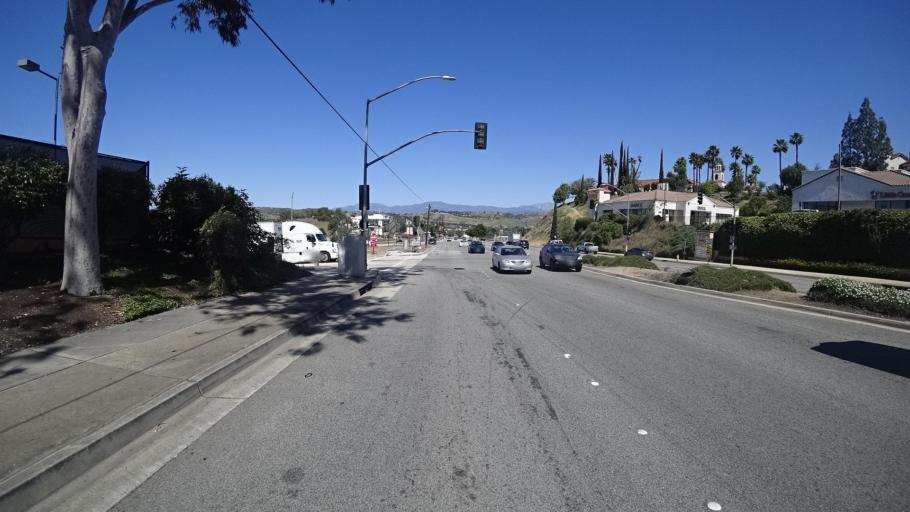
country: US
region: California
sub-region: Los Angeles County
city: Diamond Bar
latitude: 34.0416
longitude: -117.7994
